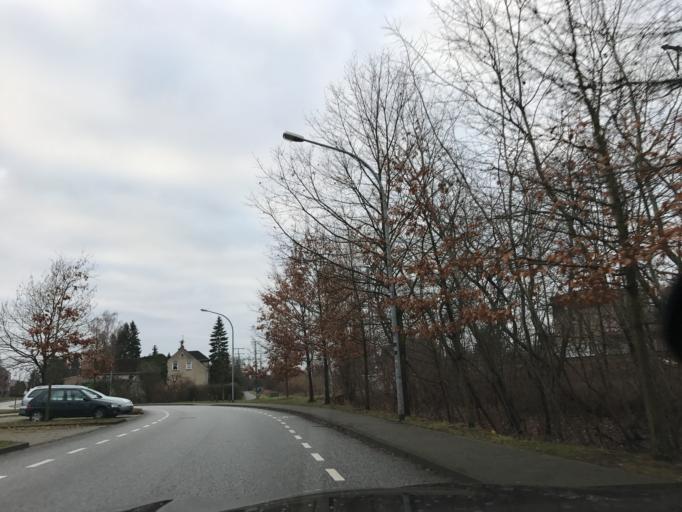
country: DE
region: Brandenburg
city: Werder
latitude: 52.4072
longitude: 12.9717
